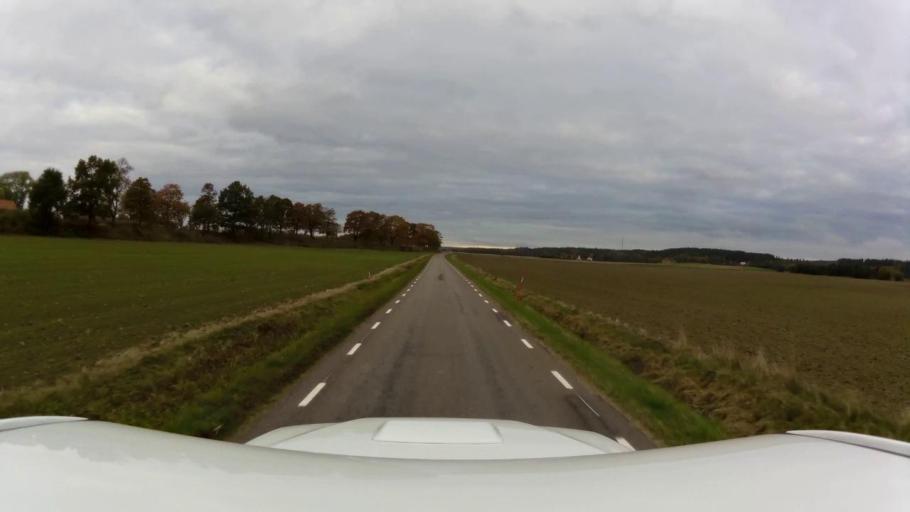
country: SE
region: OEstergoetland
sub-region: Linkopings Kommun
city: Ljungsbro
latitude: 58.5264
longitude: 15.4257
